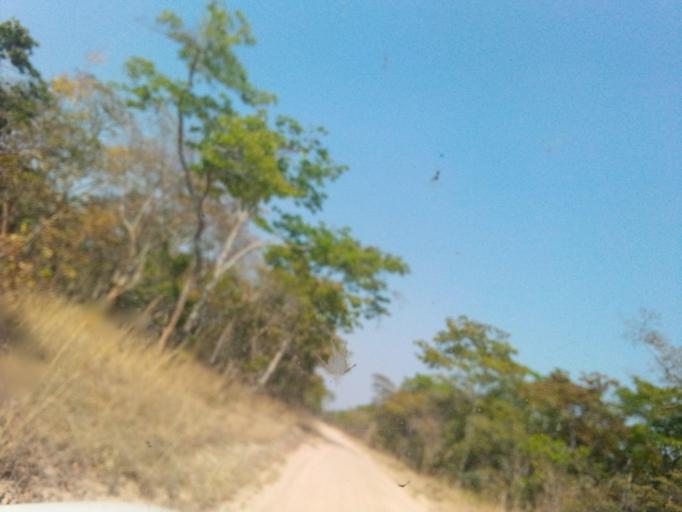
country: ZM
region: Northern
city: Mpika
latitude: -12.2264
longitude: 30.8921
